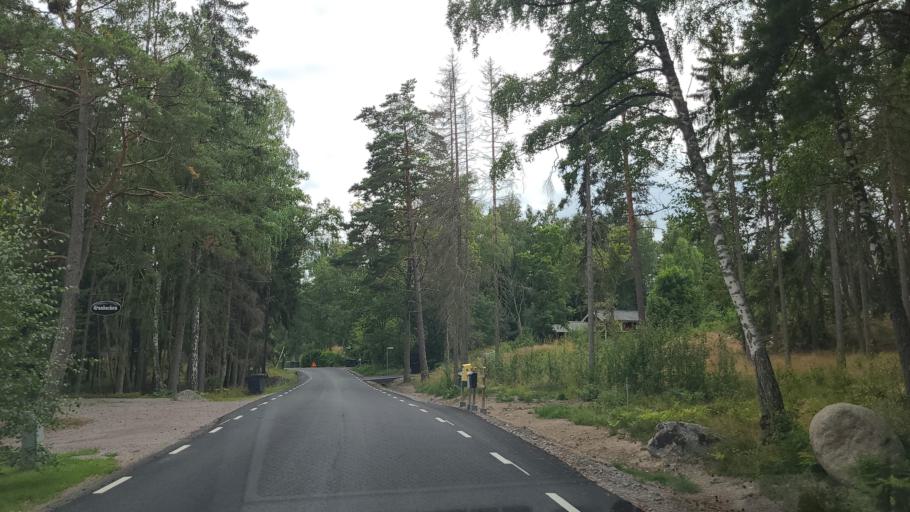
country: SE
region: Stockholm
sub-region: Upplands-Bro Kommun
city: Bro
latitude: 59.4805
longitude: 17.5979
